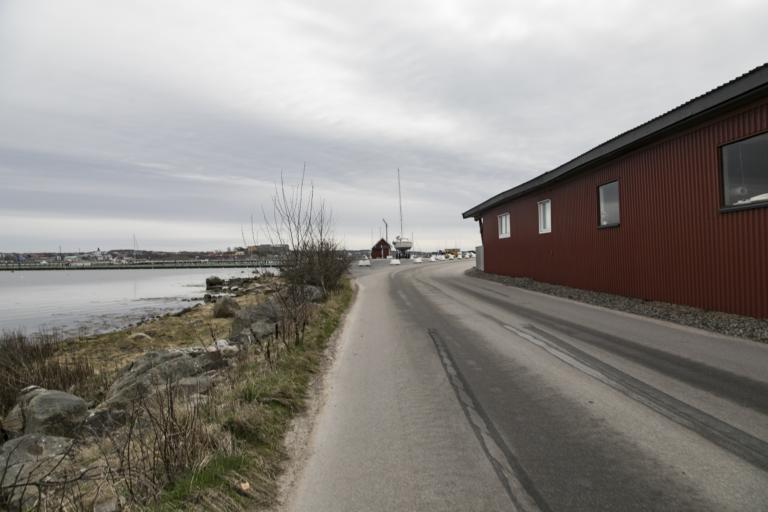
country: SE
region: Halland
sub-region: Varbergs Kommun
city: Varberg
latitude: 57.1152
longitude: 12.2254
